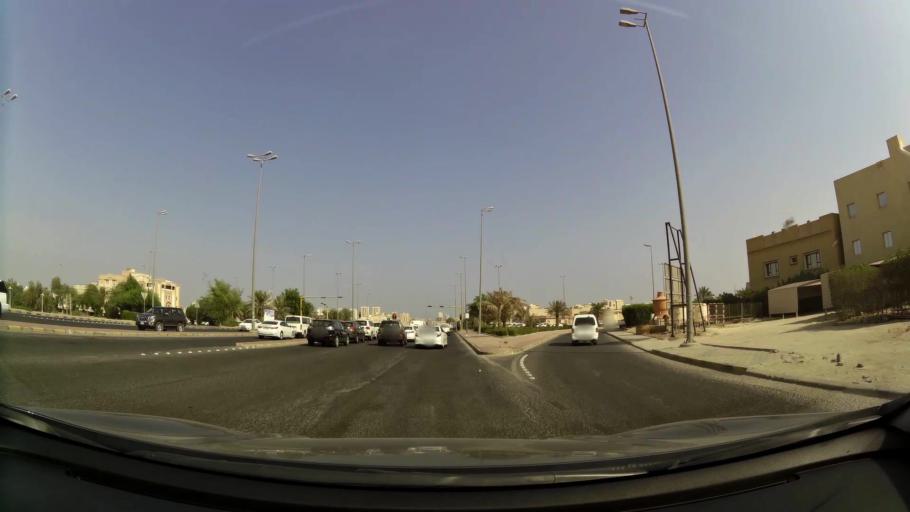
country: KW
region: Al Ahmadi
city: Ar Riqqah
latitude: 29.1339
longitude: 48.1016
